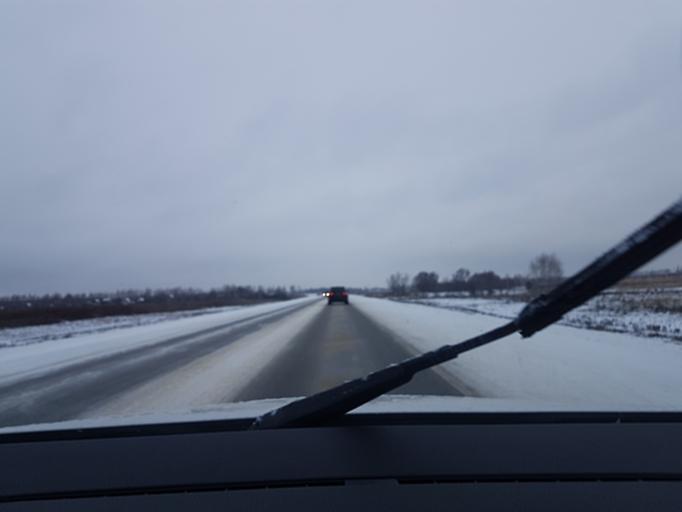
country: RU
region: Rjazan
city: Korablino
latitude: 53.7497
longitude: 39.8551
